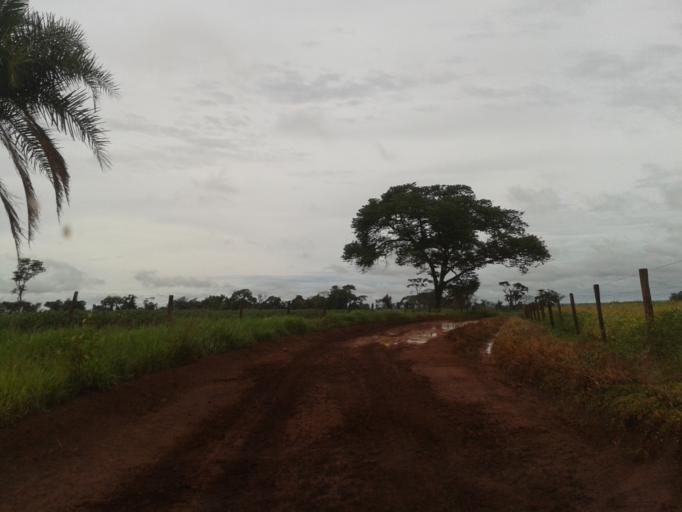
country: BR
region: Minas Gerais
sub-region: Capinopolis
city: Capinopolis
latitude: -18.7472
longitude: -49.7827
